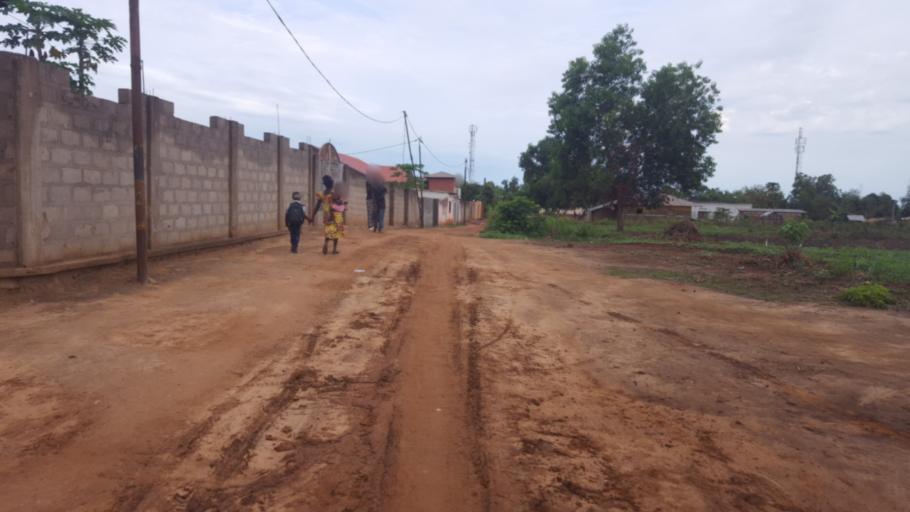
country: CD
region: Bandundu
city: Bandundu
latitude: -3.3019
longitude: 17.3778
